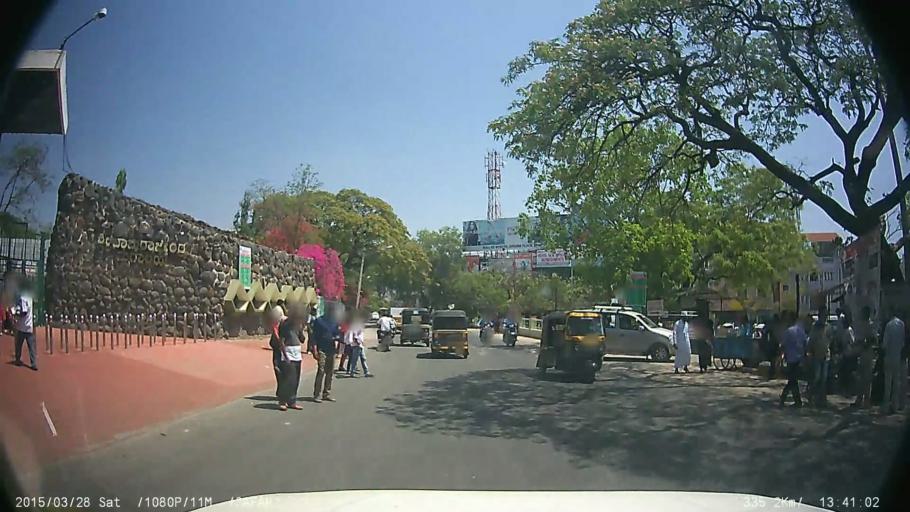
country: IN
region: Karnataka
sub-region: Mysore
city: Mysore
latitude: 12.3025
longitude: 76.6636
